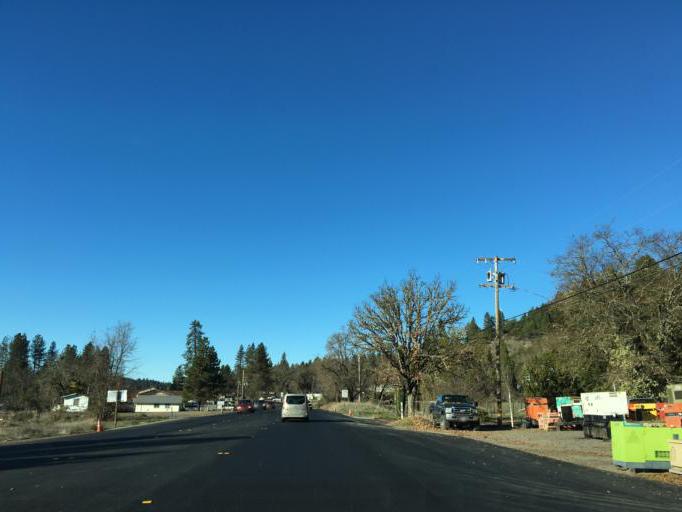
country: US
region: California
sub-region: Mendocino County
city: Laytonville
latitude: 39.6820
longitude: -123.4768
